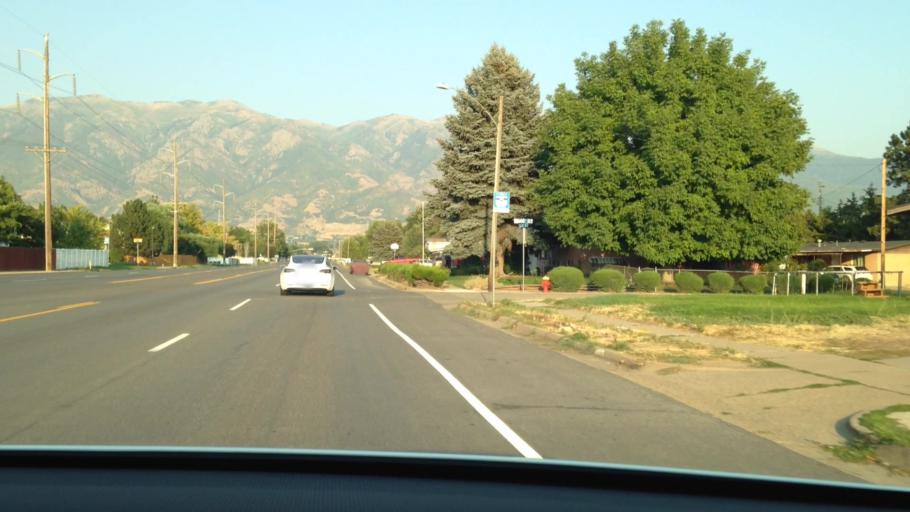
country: US
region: Utah
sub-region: Davis County
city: Layton
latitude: 41.0763
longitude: -111.9667
